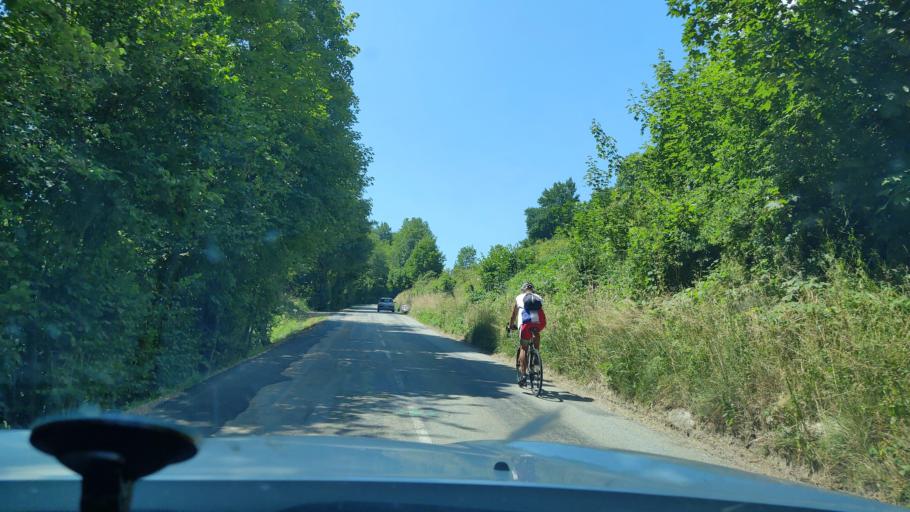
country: FR
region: Rhone-Alpes
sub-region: Departement de la Savoie
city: Mery
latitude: 45.6551
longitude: 6.0290
